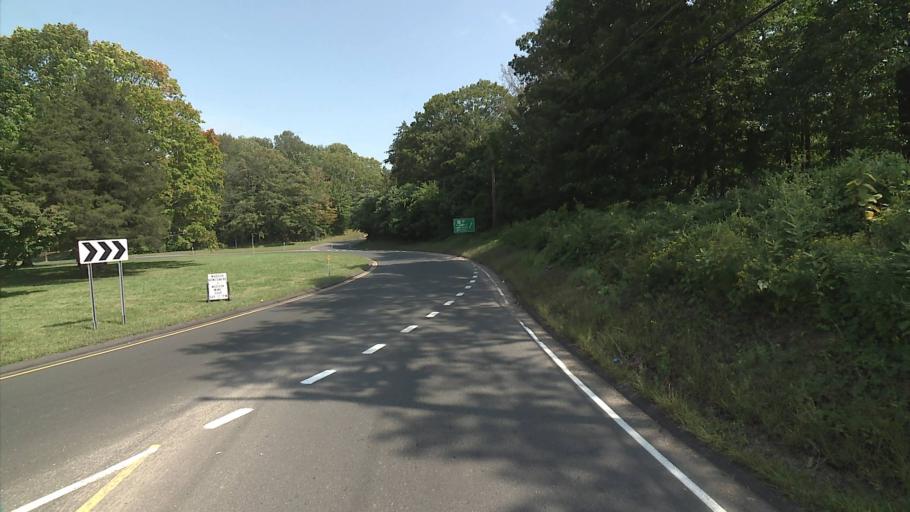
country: US
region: Connecticut
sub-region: New Haven County
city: Guilford
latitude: 41.3593
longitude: -72.6379
